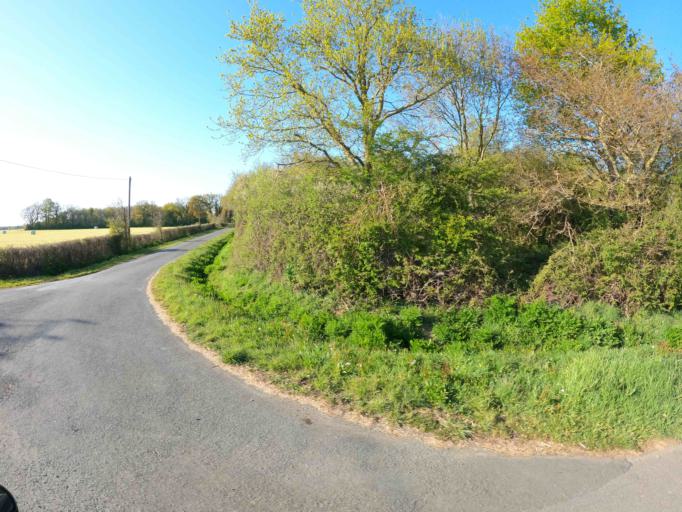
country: FR
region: Pays de la Loire
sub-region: Departement de la Vendee
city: Les Brouzils
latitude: 46.8917
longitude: -1.3599
